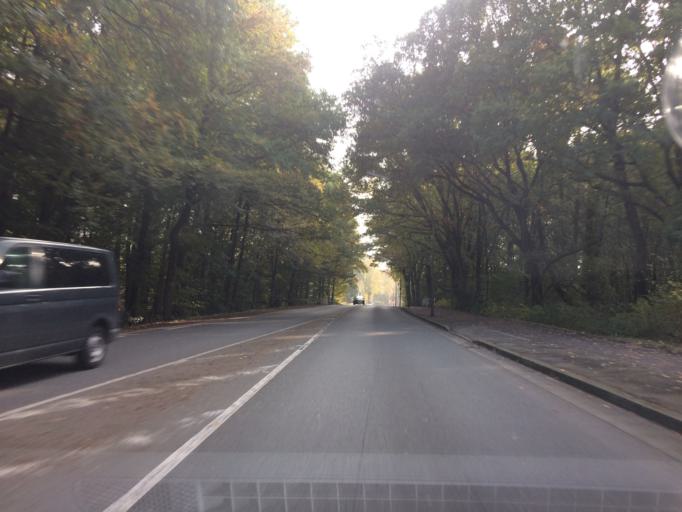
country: DE
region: North Rhine-Westphalia
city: Marl
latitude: 51.6715
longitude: 7.0766
